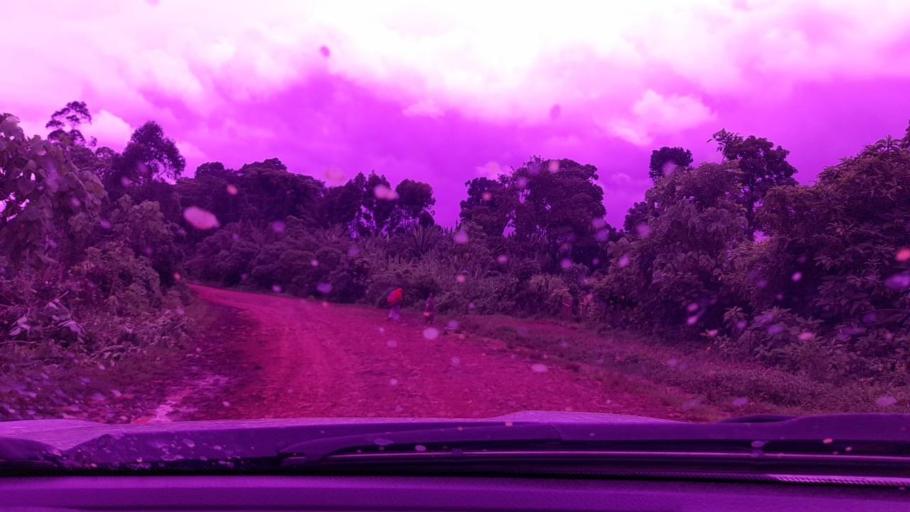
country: ET
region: Southern Nations, Nationalities, and People's Region
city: Tippi
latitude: 7.5714
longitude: 35.6496
